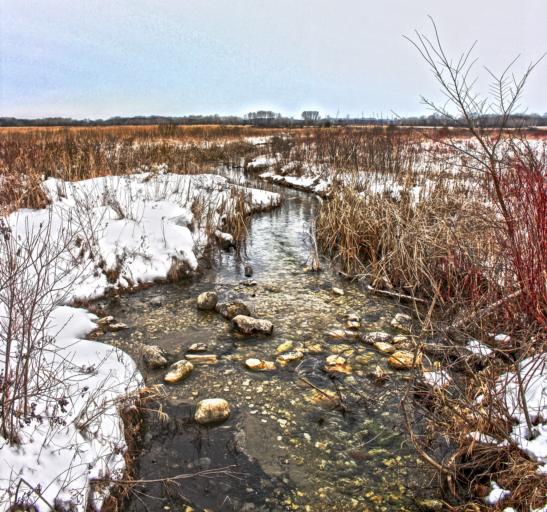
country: US
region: Wisconsin
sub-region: Waukesha County
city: Eagle
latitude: 42.9332
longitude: -88.4705
